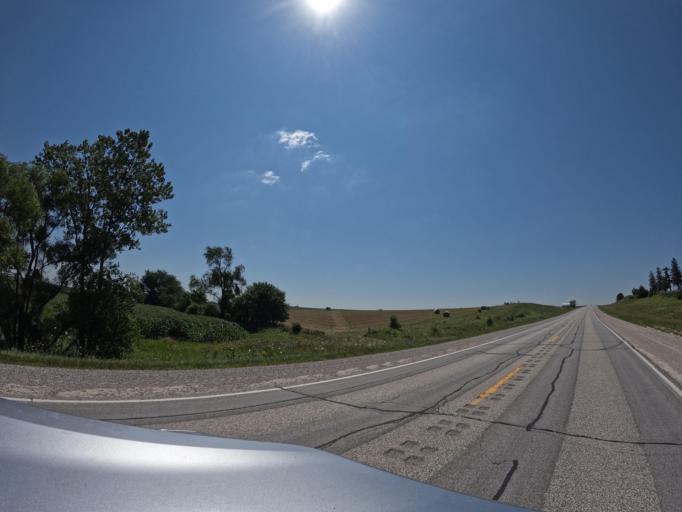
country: US
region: Iowa
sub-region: Keokuk County
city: Sigourney
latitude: 41.2796
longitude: -92.2044
